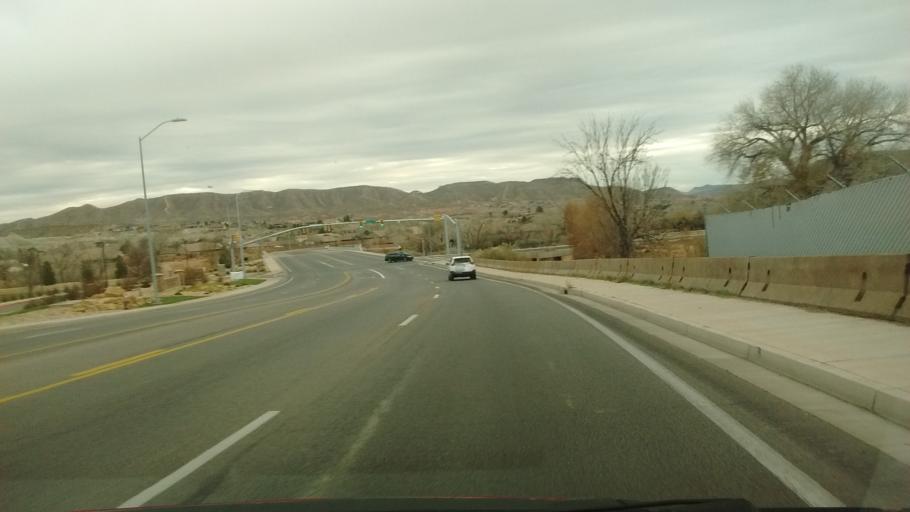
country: US
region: Utah
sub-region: Washington County
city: Washington
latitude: 37.1178
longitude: -113.5035
